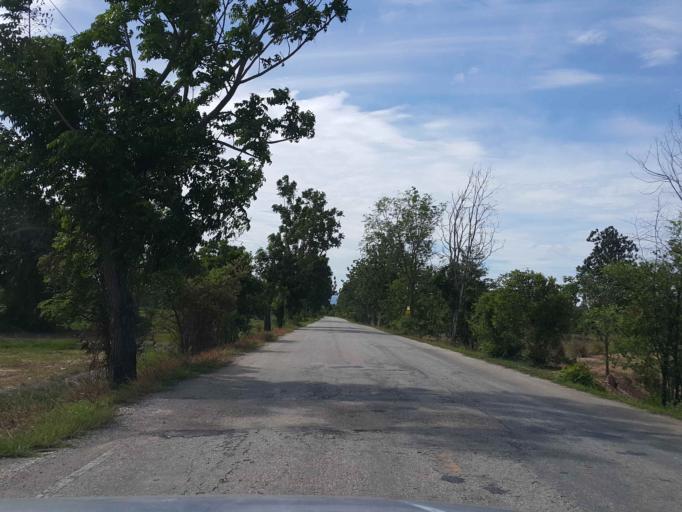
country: TH
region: Sukhothai
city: Ban Dan Lan Hoi
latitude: 17.1275
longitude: 99.5297
